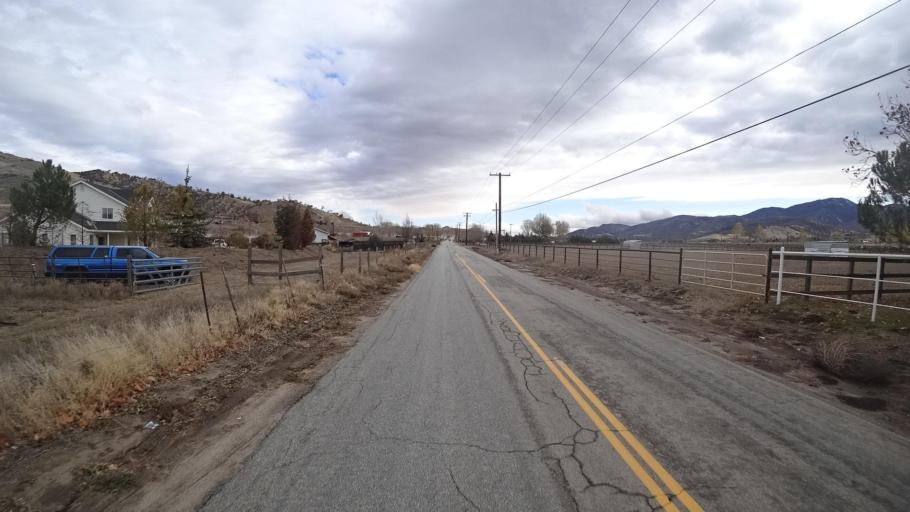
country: US
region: California
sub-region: Kern County
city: Golden Hills
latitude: 35.1173
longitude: -118.5408
